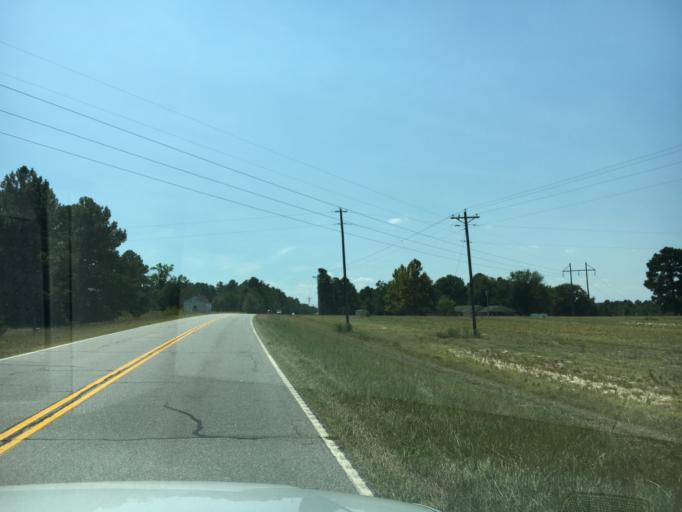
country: US
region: South Carolina
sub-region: Lexington County
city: Batesburg
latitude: 33.7736
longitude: -81.6407
